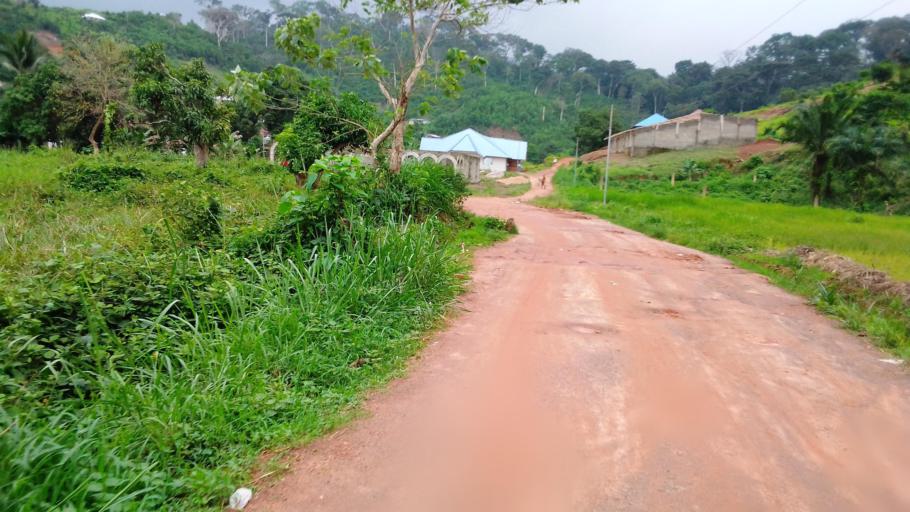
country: SL
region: Eastern Province
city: Kenema
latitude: 7.8799
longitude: -11.1980
